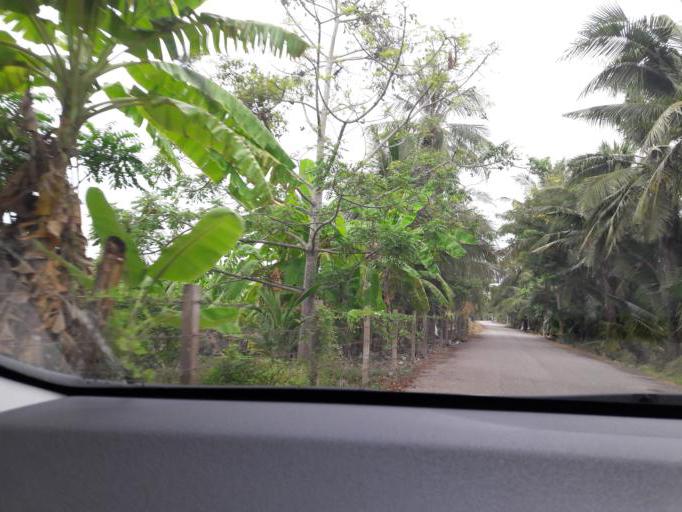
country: TH
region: Samut Sakhon
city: Ban Phaeo
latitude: 13.5674
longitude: 100.0303
